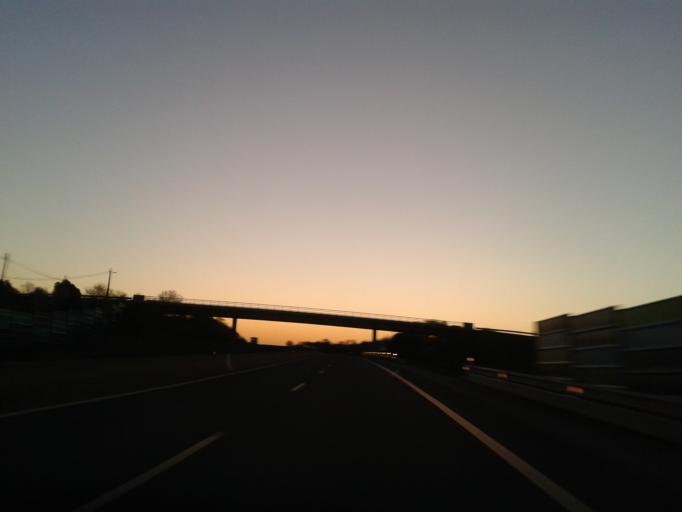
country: PT
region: Faro
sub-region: Albufeira
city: Guia
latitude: 37.1370
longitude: -8.3007
